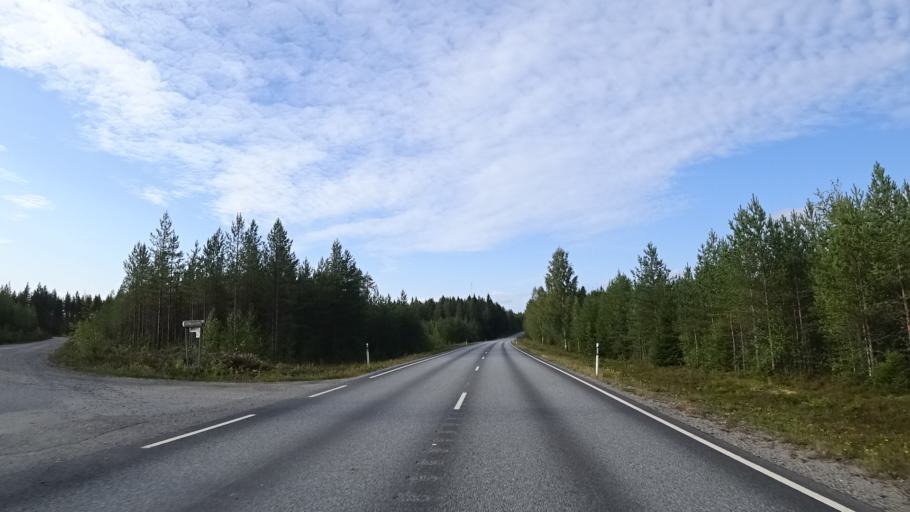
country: FI
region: North Karelia
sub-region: Joensuu
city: Eno
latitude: 62.8491
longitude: 30.1926
